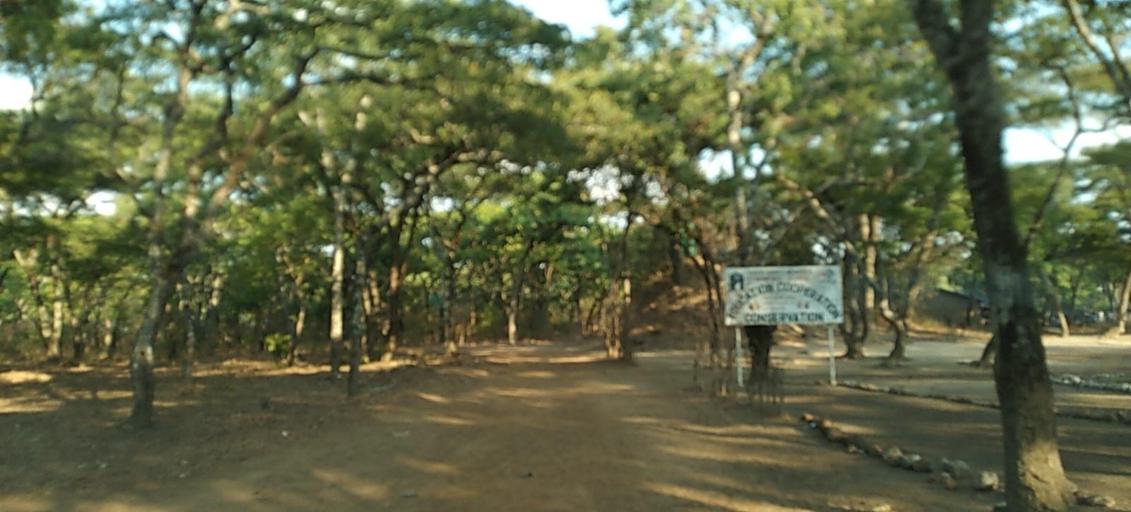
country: ZM
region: Copperbelt
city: Chililabombwe
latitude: -12.3675
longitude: 27.4800
